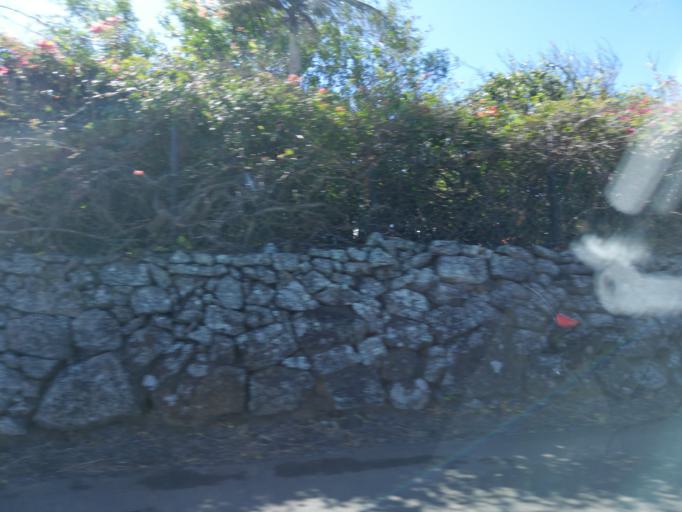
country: MU
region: Grand Port
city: Beau Vallon
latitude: -20.4444
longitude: 57.6943
